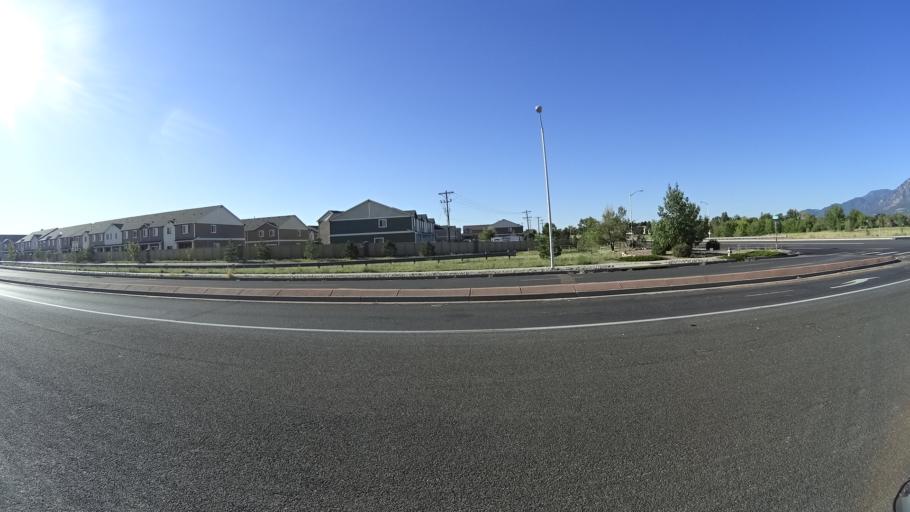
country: US
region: Colorado
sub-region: El Paso County
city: Stratmoor
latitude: 38.7891
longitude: -104.7384
